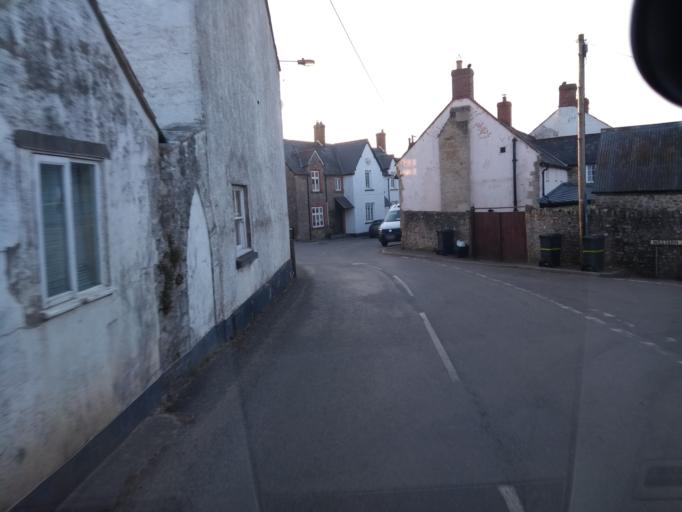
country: GB
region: England
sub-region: Somerset
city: Ilminster
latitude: 50.8540
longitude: -2.8907
